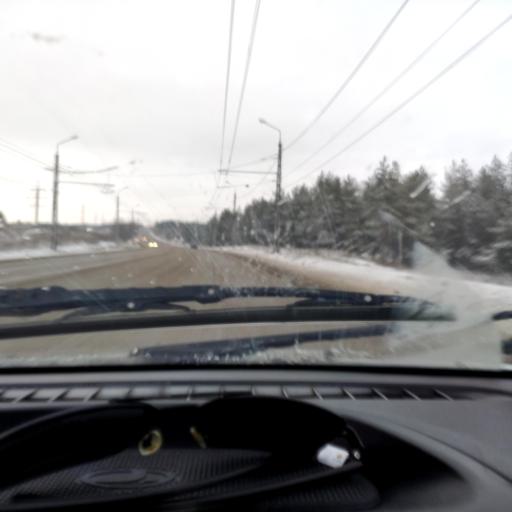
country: RU
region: Samara
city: Zhigulevsk
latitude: 53.4999
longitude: 49.5126
